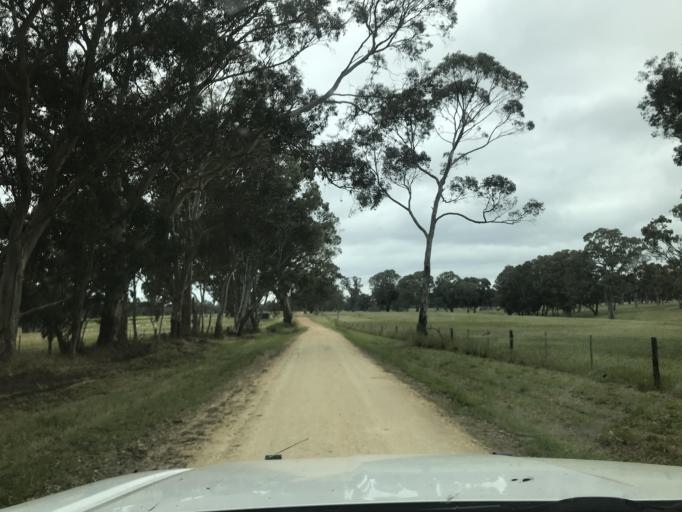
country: AU
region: South Australia
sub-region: Wattle Range
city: Penola
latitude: -37.2730
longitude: 140.9809
